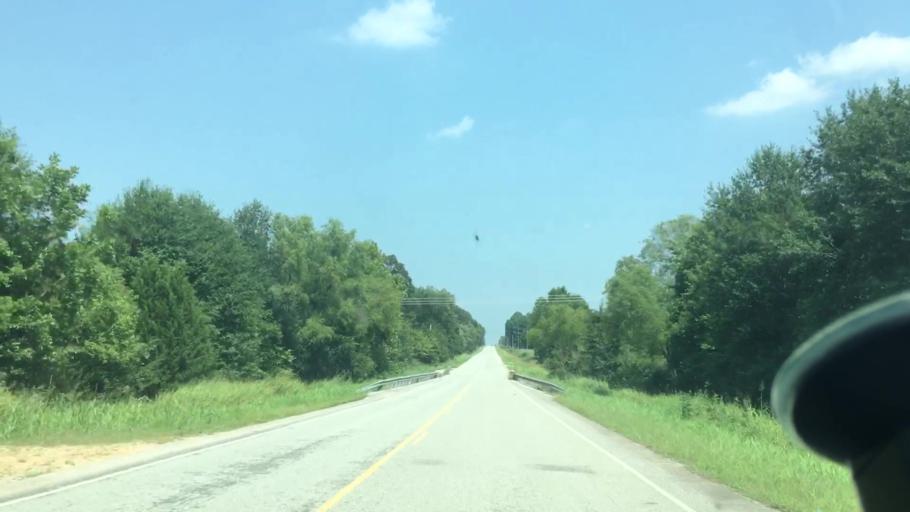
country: US
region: Oklahoma
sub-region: Atoka County
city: Atoka
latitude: 34.2566
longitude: -95.9361
